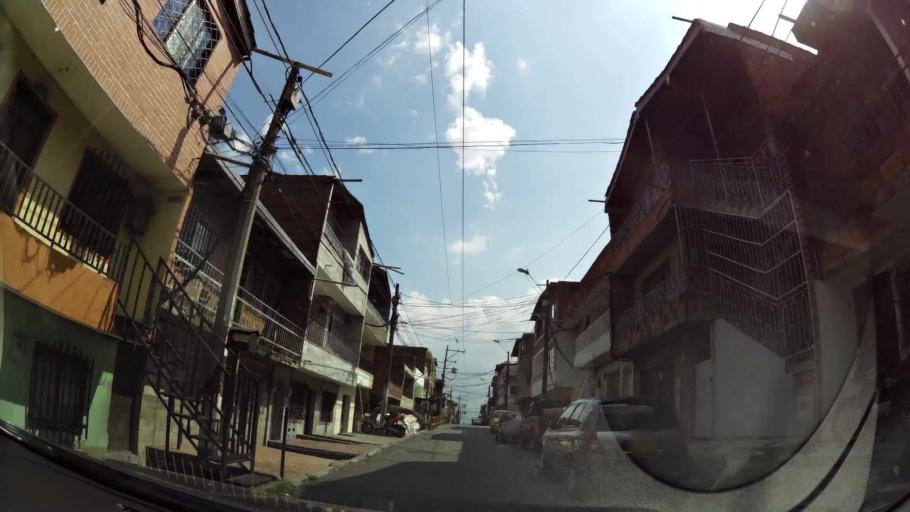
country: CO
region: Antioquia
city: Medellin
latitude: 6.2879
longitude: -75.5811
